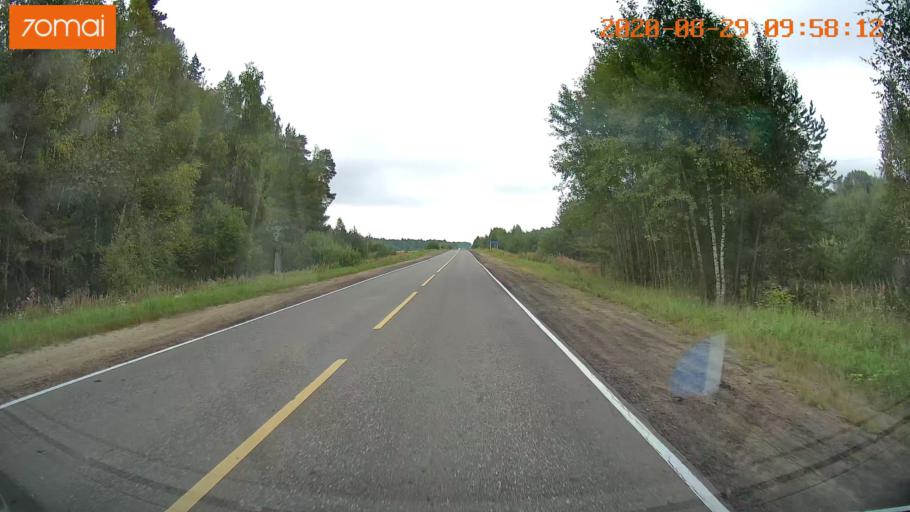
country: RU
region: Ivanovo
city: Zarechnyy
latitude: 57.4141
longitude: 42.3334
